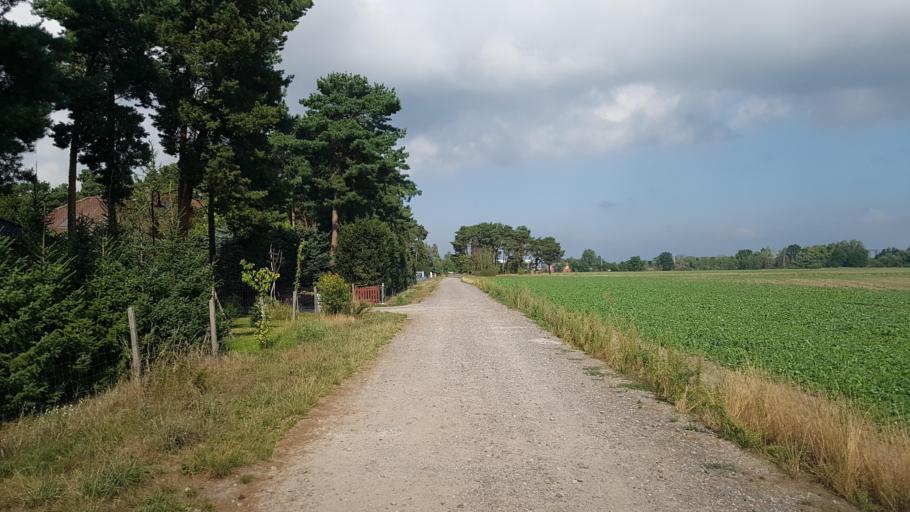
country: DE
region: Brandenburg
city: Bruck
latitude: 52.1838
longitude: 12.7652
